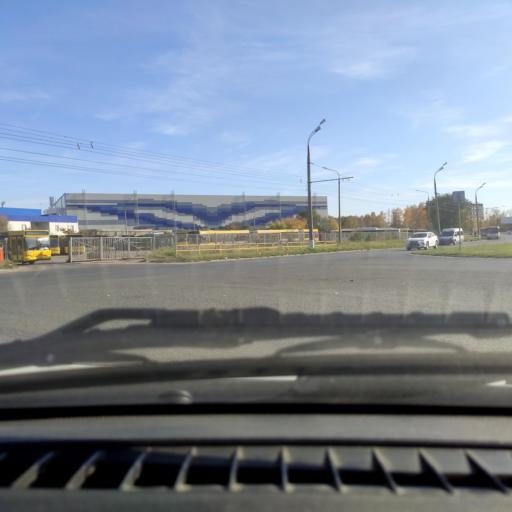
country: RU
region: Samara
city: Tol'yatti
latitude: 53.5067
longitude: 49.2543
